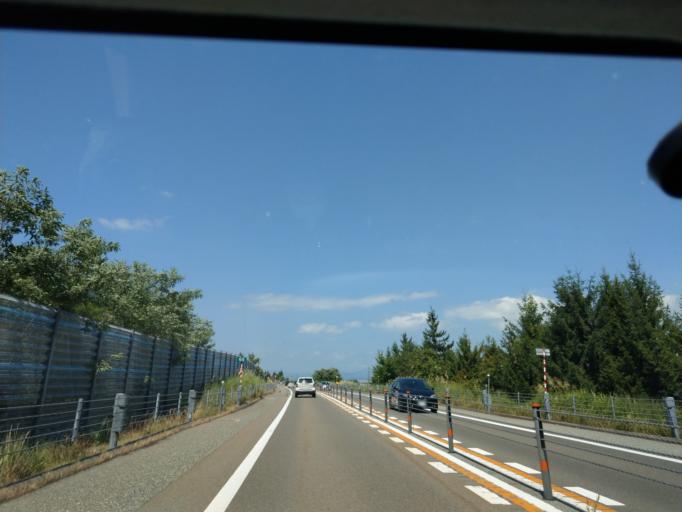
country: JP
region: Akita
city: Omagari
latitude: 39.3907
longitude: 140.4787
